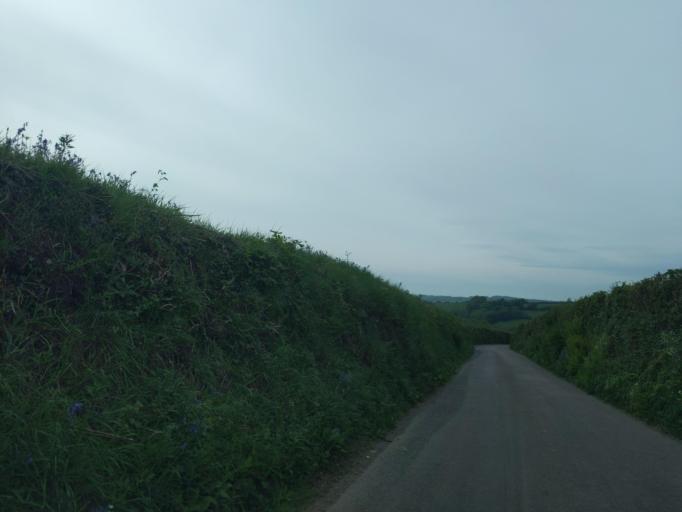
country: GB
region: England
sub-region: Devon
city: Plympton
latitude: 50.4302
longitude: -4.0515
